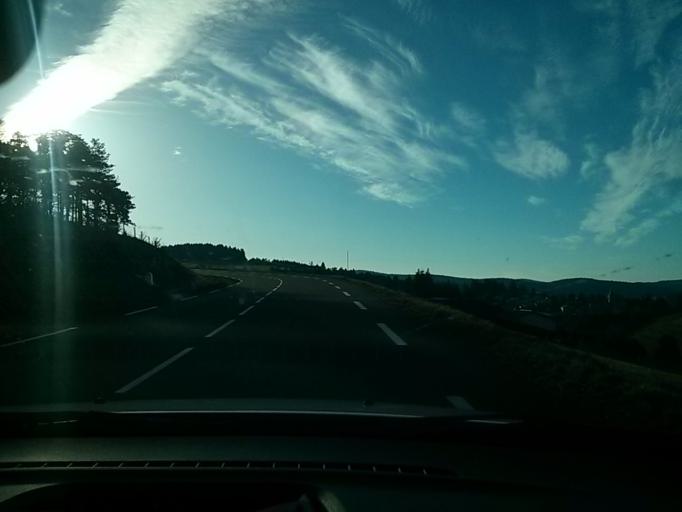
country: FR
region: Rhone-Alpes
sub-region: Departement de la Loire
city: Saint-Genest-Malifaux
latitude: 45.3790
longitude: 4.4909
